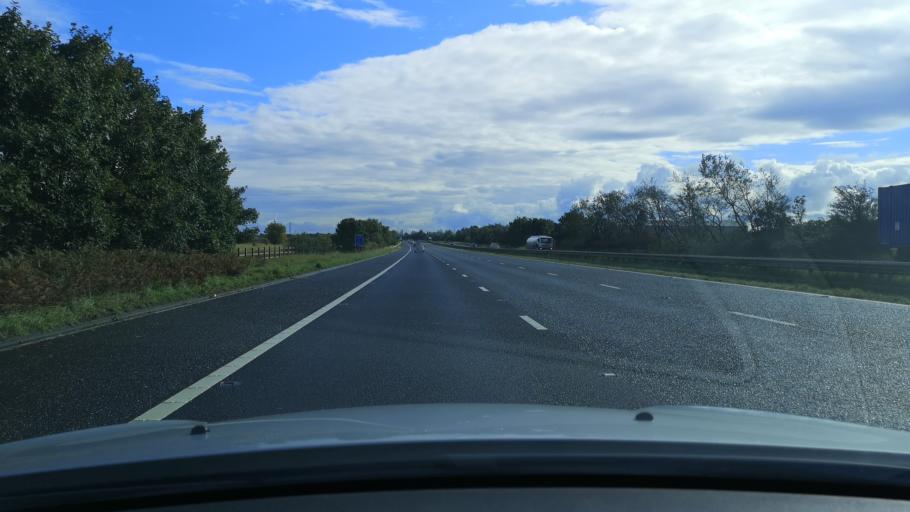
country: GB
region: England
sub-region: East Riding of Yorkshire
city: Pollington
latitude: 53.6868
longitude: -1.0929
